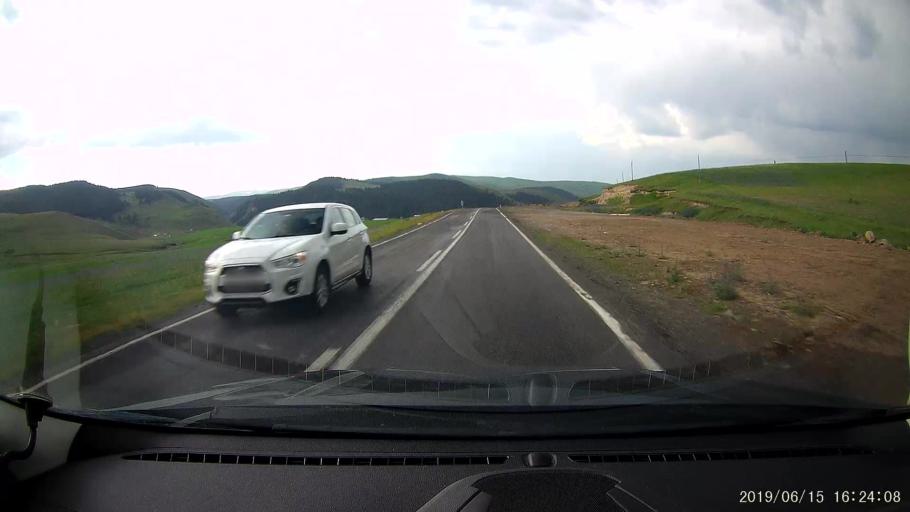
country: TR
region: Ardahan
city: Hanak
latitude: 41.1686
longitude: 42.8684
